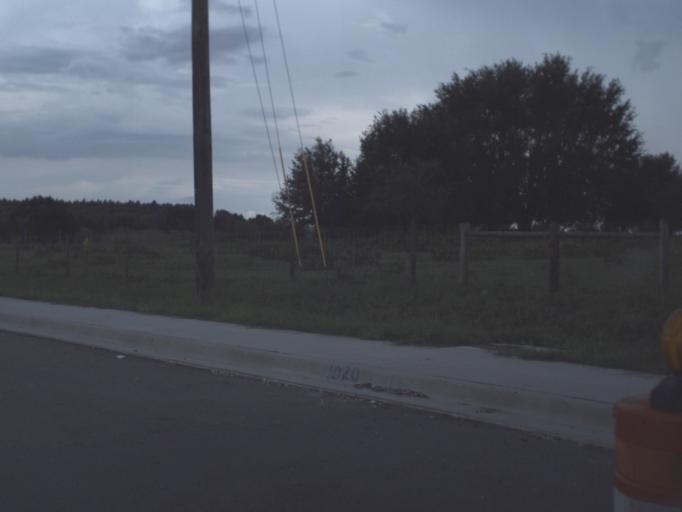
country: US
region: Florida
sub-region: Polk County
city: Polk City
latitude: 28.1529
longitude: -81.8013
